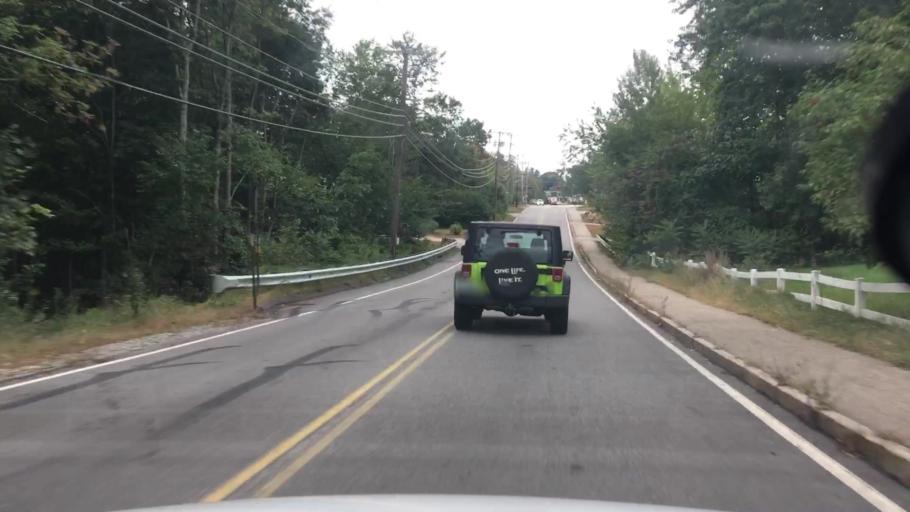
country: US
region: New Hampshire
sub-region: Strafford County
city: Rochester
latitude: 43.2918
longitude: -70.9702
